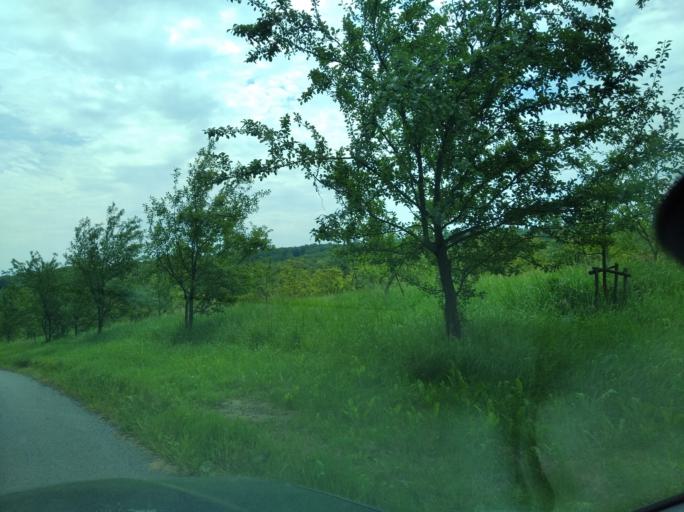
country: PL
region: Subcarpathian Voivodeship
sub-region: Powiat przeworski
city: Lopuszka Wielka
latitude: 49.9026
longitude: 22.4113
